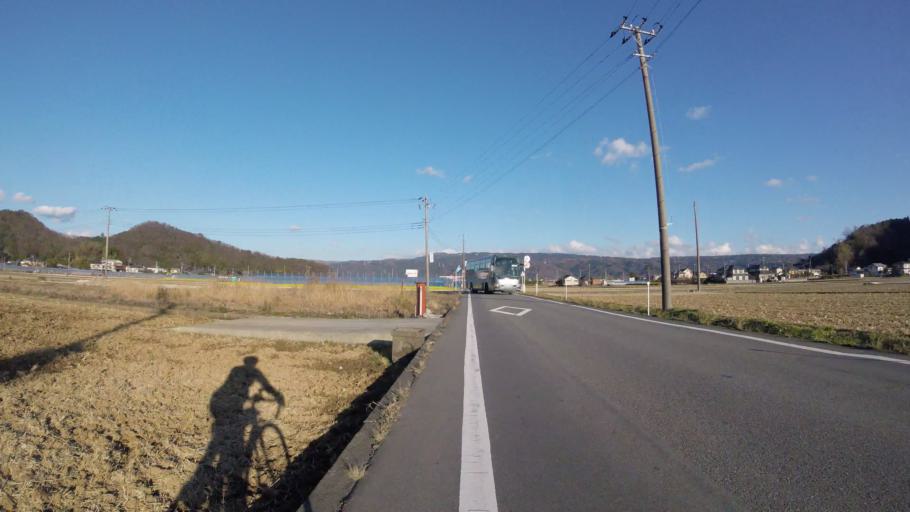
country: JP
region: Shizuoka
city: Mishima
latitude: 35.0565
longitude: 138.9261
